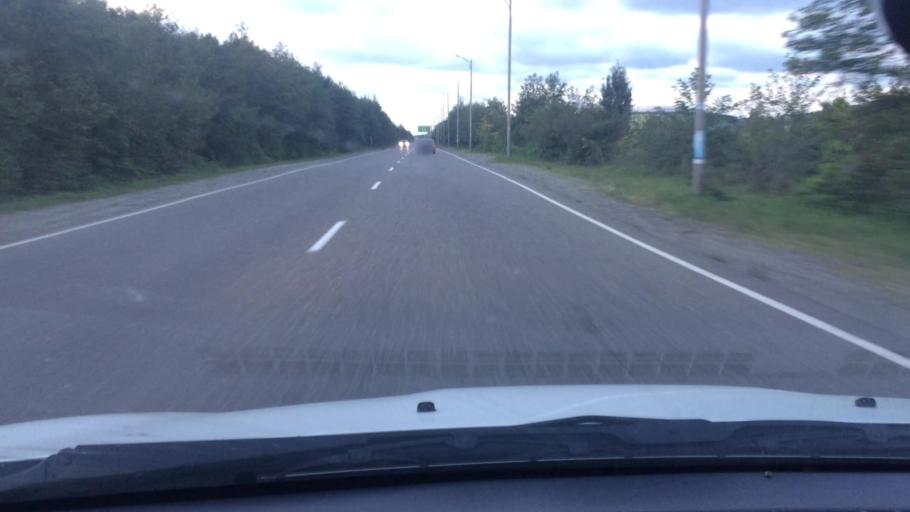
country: GE
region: Guria
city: Urek'i
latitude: 41.9300
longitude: 41.7727
